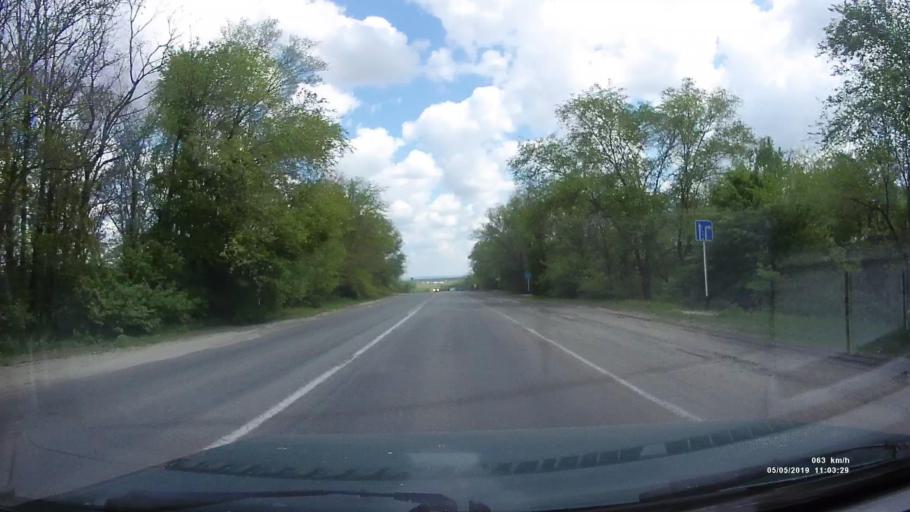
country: RU
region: Rostov
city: Ust'-Donetskiy
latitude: 47.6921
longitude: 40.9210
